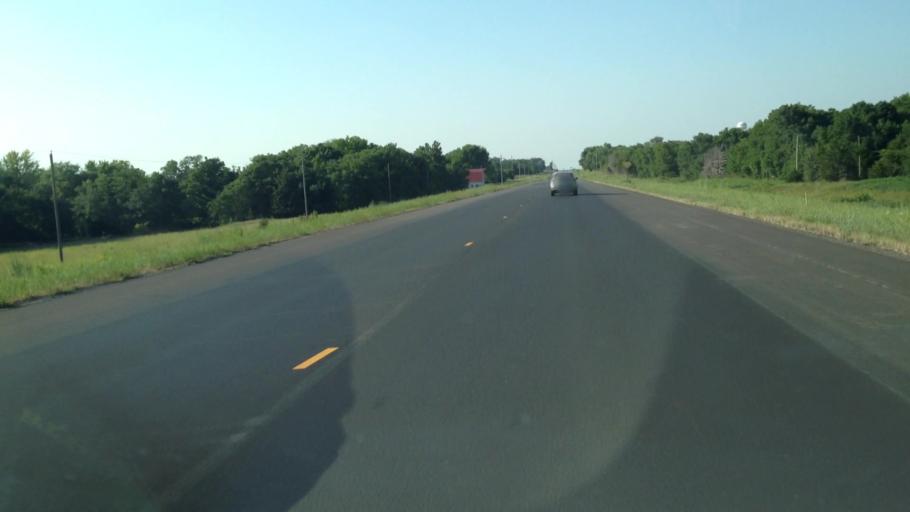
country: US
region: Kansas
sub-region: Franklin County
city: Ottawa
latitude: 38.4791
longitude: -95.2673
